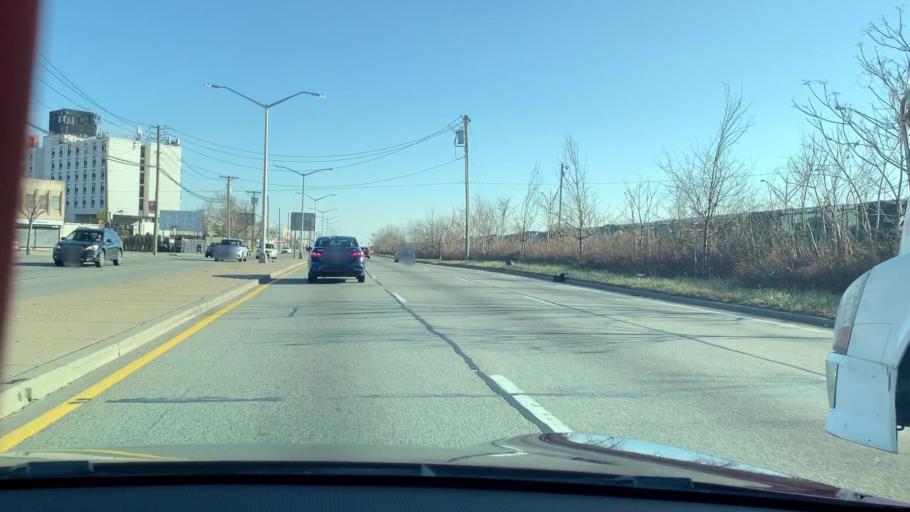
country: US
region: New York
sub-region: Nassau County
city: Inwood
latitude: 40.6584
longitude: -73.7715
